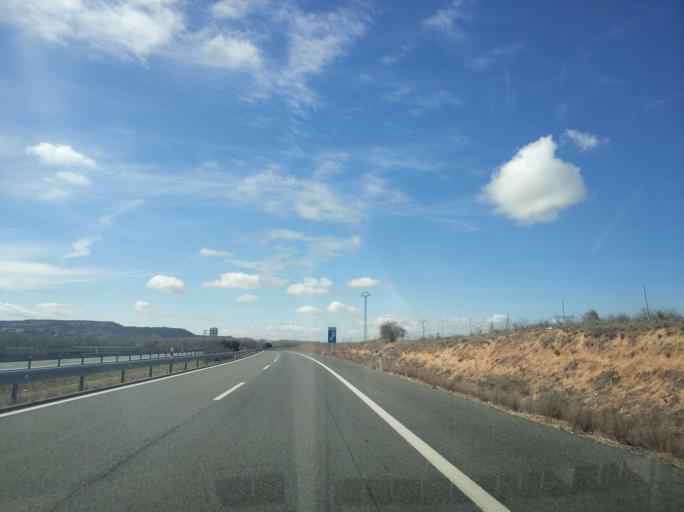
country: ES
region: Castille and Leon
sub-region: Provincia de Burgos
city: Celada del Camino
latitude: 42.2612
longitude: -3.9421
